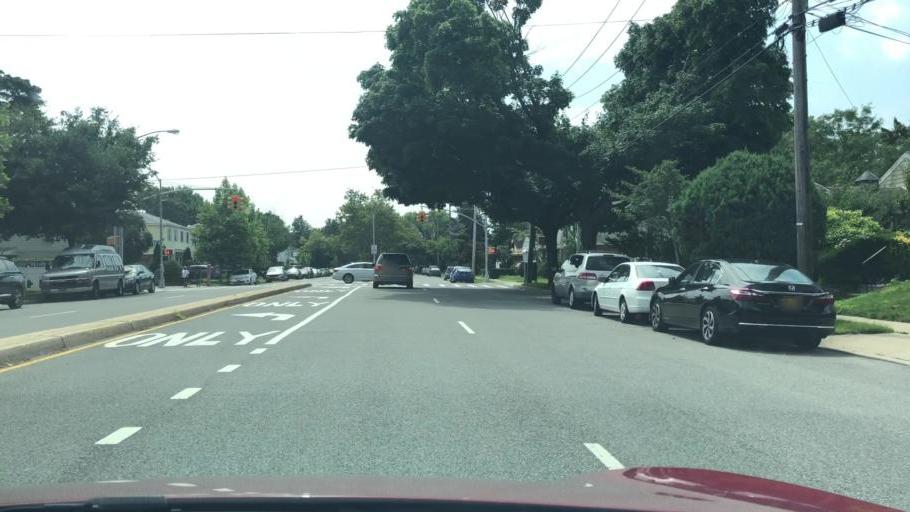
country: US
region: New York
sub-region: Nassau County
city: Bellerose Terrace
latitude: 40.7465
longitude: -73.7611
